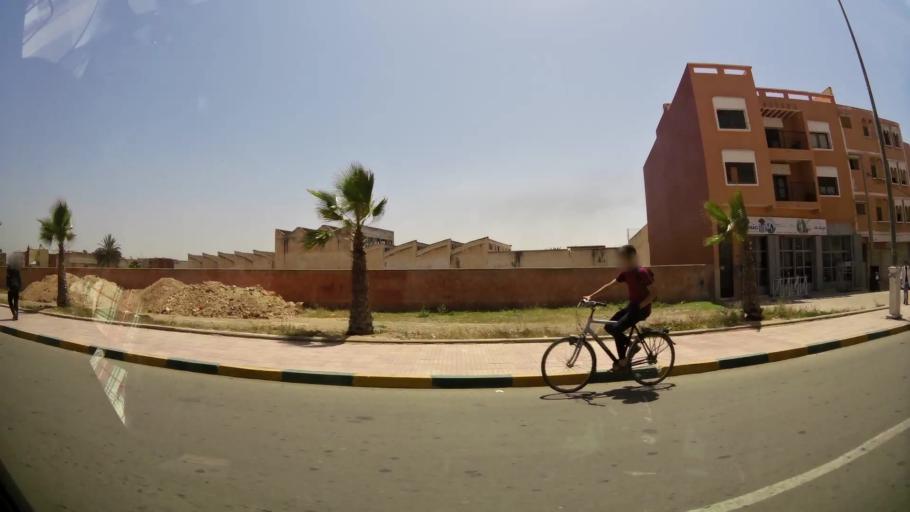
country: MA
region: Souss-Massa-Draa
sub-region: Inezgane-Ait Mellou
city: Inezgane
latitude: 30.3522
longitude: -9.4919
